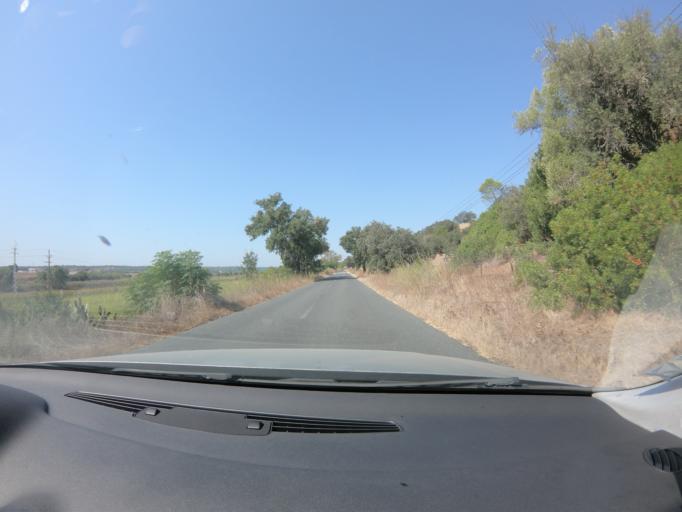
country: PT
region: Setubal
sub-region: Alcacer do Sal
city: Alcacer do Sal
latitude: 38.2725
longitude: -8.3640
